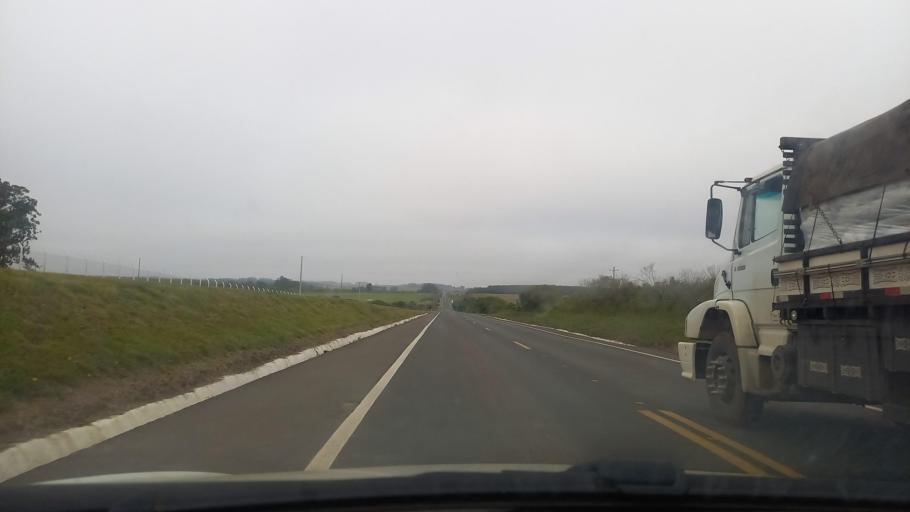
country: BR
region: Rio Grande do Sul
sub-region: Rosario Do Sul
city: Rosario do Sul
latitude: -30.2798
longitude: -54.9806
